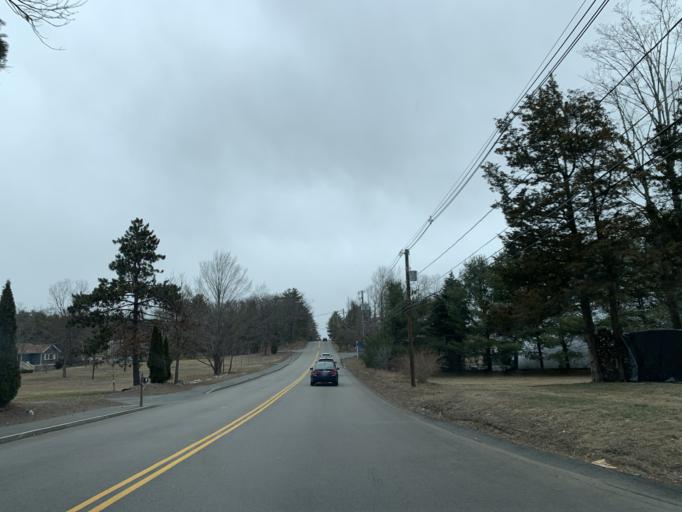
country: US
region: Massachusetts
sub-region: Norfolk County
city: Franklin
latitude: 42.1000
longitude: -71.3722
